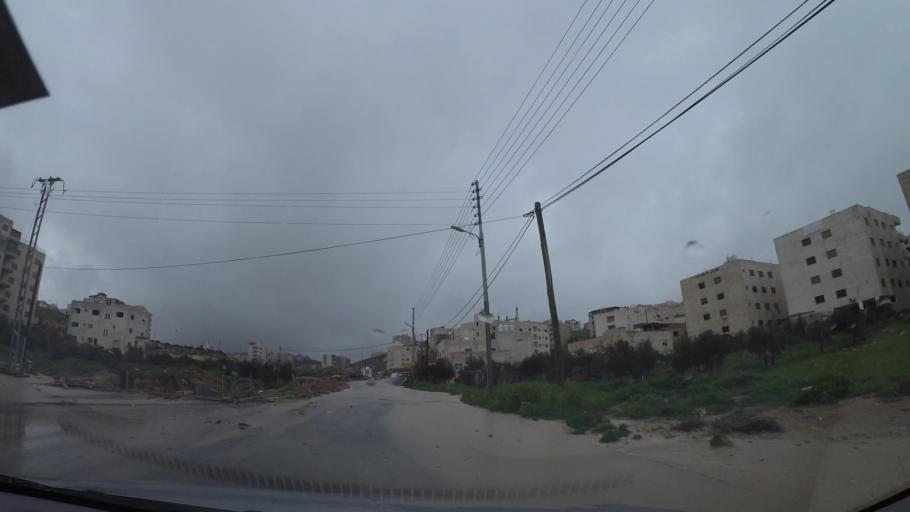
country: JO
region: Amman
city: Al Jubayhah
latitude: 32.0396
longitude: 35.8929
